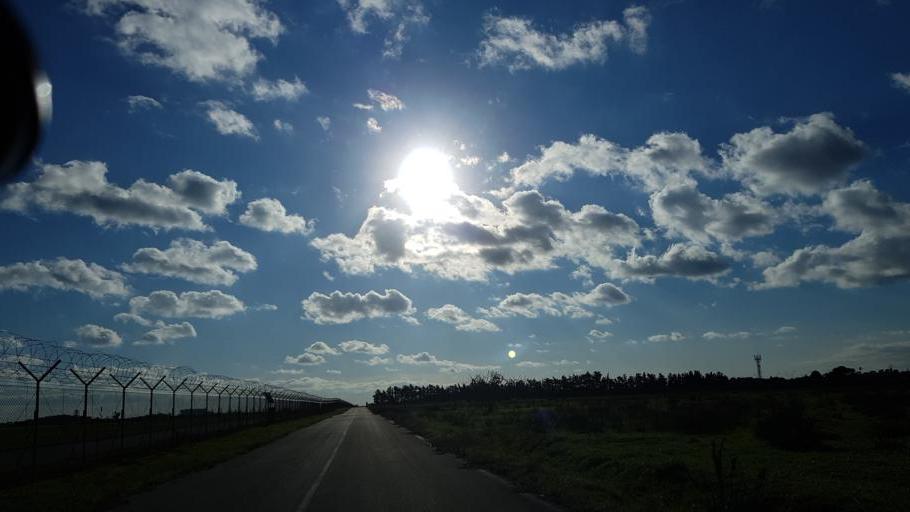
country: IT
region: Apulia
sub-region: Provincia di Brindisi
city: Materdomini
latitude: 40.6703
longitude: 17.9294
